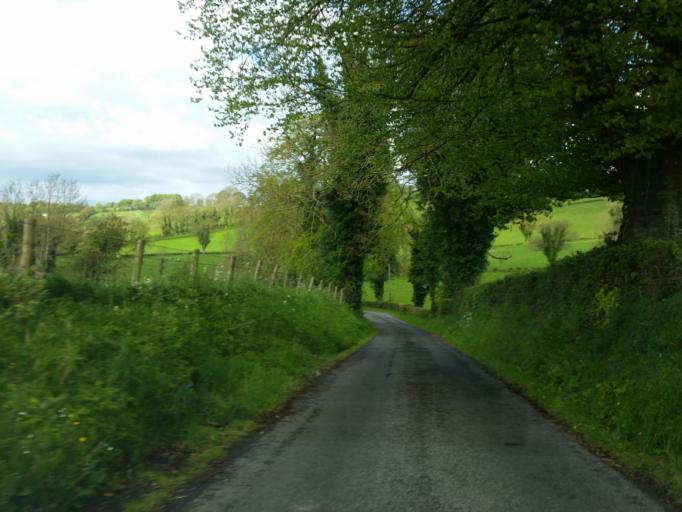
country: GB
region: Northern Ireland
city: Lisnaskea
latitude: 54.2562
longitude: -7.4106
